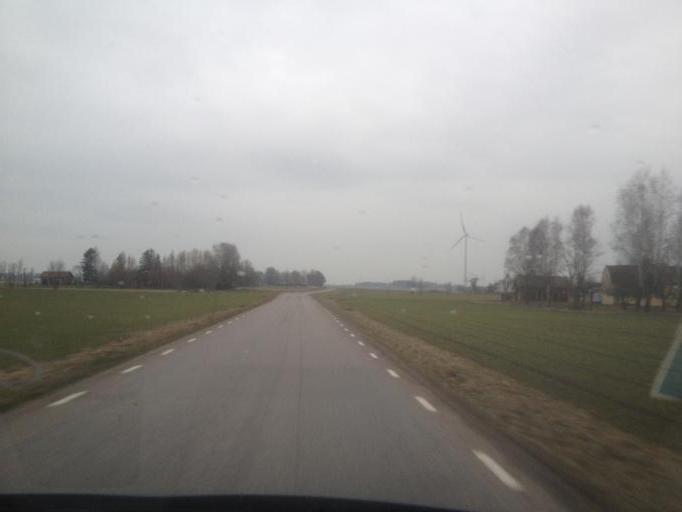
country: SE
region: OEstergoetland
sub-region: Linkopings Kommun
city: Vikingstad
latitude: 58.4297
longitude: 15.3649
